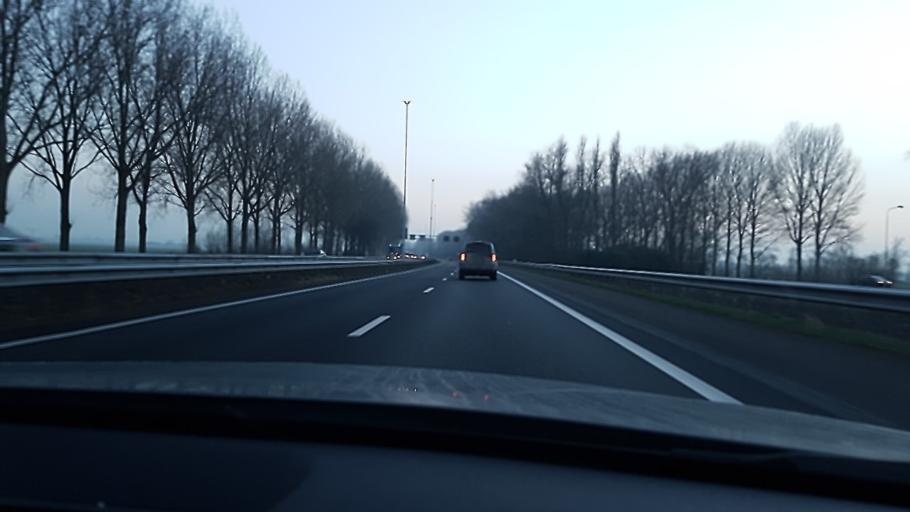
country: NL
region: North Brabant
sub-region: Gemeente Oosterhout
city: Oosterhout
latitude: 51.6735
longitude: 4.8798
